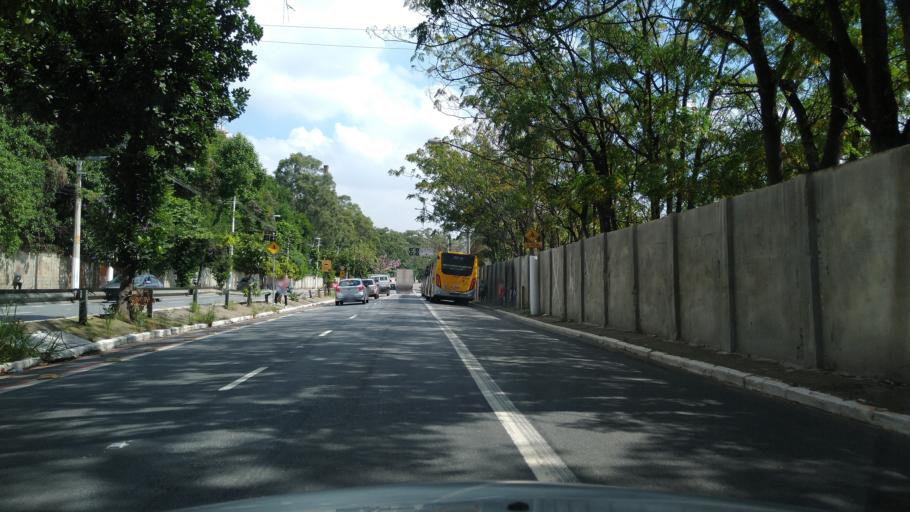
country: BR
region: Sao Paulo
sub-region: Guarulhos
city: Guarulhos
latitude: -23.4835
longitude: -46.4950
